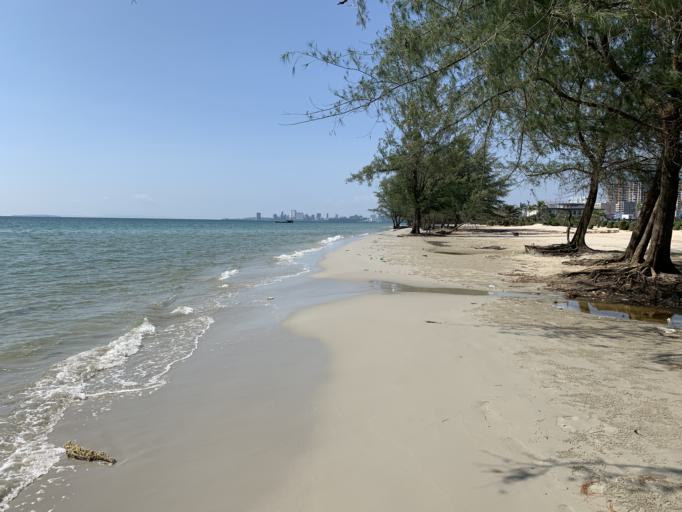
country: KH
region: Preah Sihanouk
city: Sihanoukville
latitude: 10.5626
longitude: 103.5568
